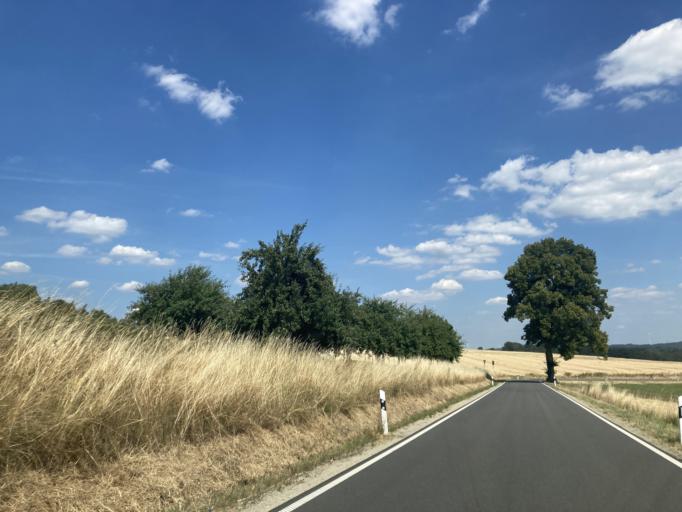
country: DE
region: Hesse
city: Grebenau
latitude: 50.7239
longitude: 9.4054
